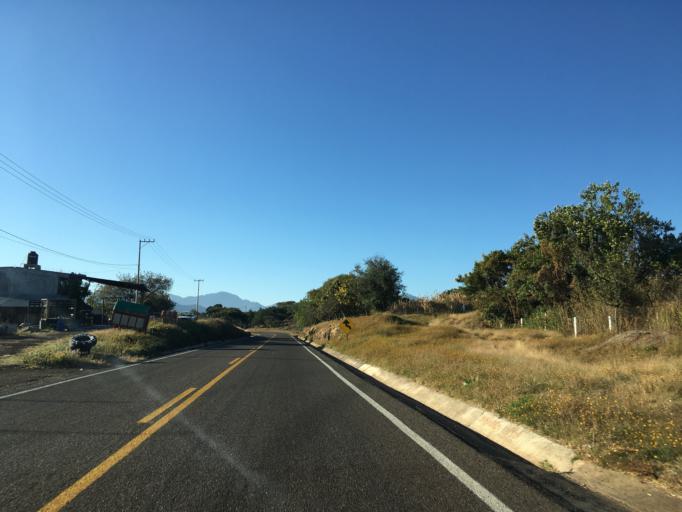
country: MX
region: Michoacan
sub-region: Tuxpan
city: La Soledad
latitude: 19.4930
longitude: -100.4535
